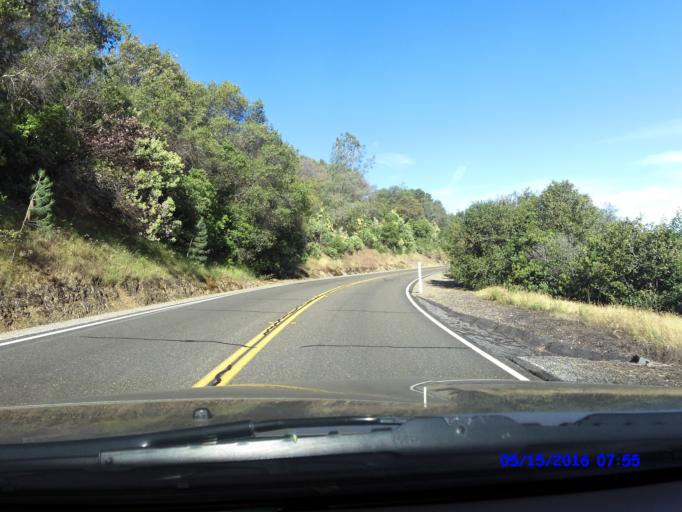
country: US
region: California
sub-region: Mariposa County
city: Mariposa
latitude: 37.5952
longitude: -120.1237
